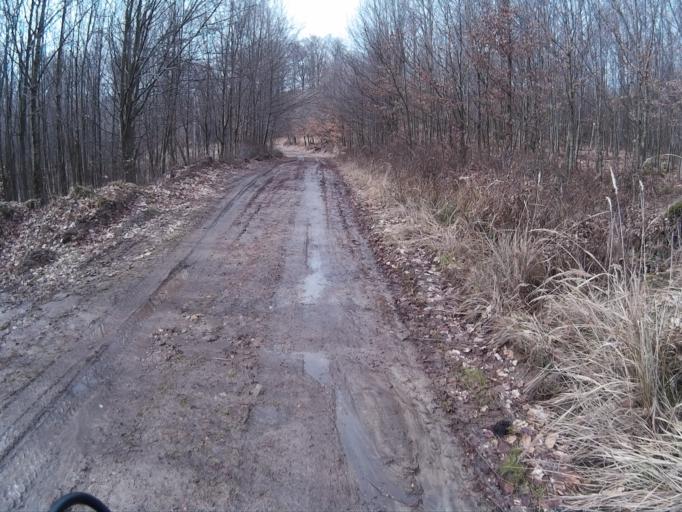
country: HU
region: Borsod-Abauj-Zemplen
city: Tolcsva
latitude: 48.4070
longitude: 21.4376
